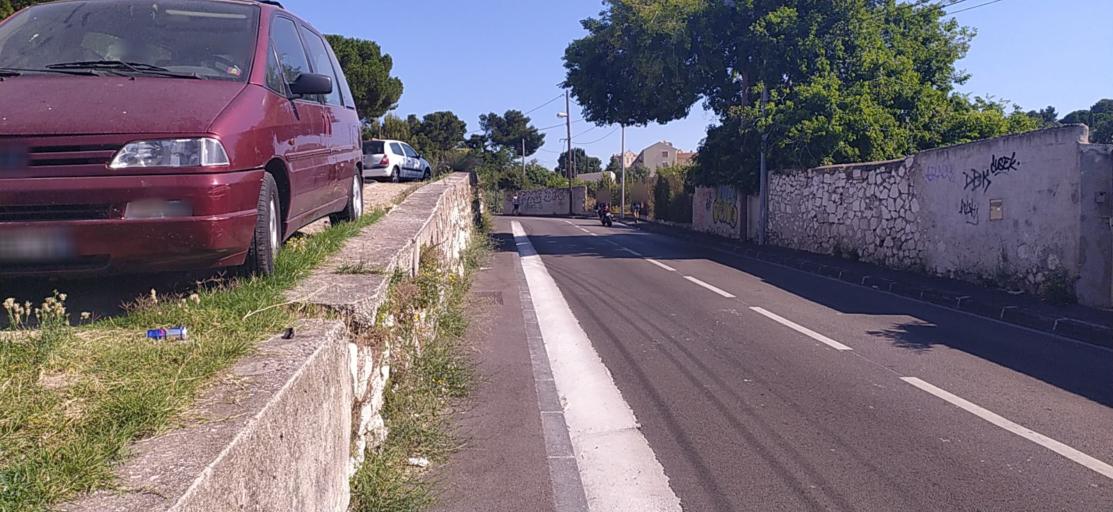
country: FR
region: Provence-Alpes-Cote d'Azur
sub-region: Departement des Bouches-du-Rhone
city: Marseille 16
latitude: 43.3379
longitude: 5.3521
